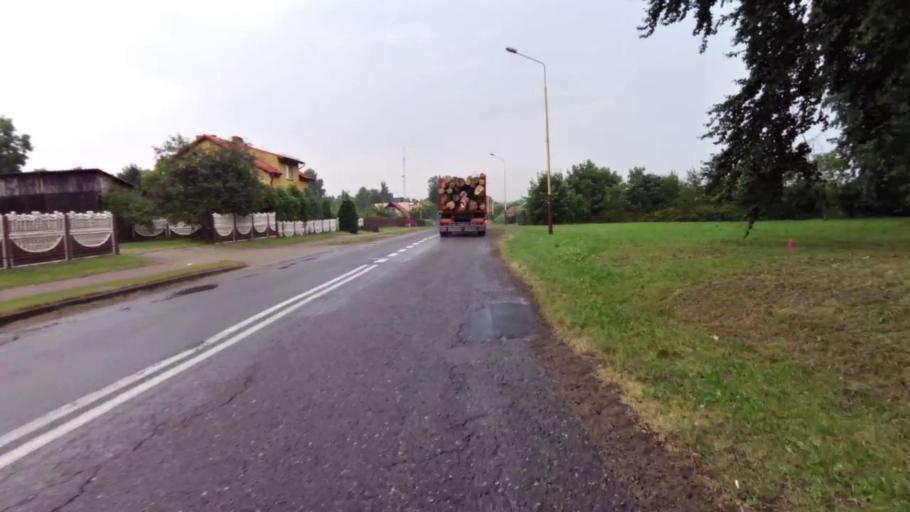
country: PL
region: West Pomeranian Voivodeship
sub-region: Powiat stargardzki
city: Insko
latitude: 53.4384
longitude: 15.5539
